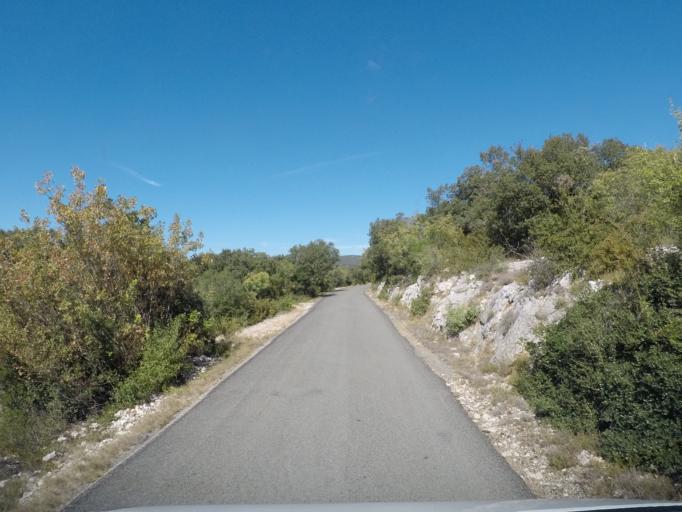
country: FR
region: Languedoc-Roussillon
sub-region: Departement de l'Herault
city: Vailhauques
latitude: 43.7219
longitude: 3.6763
